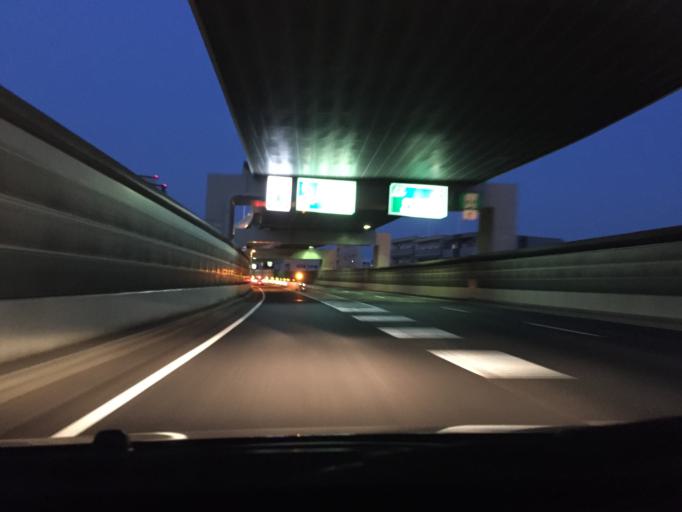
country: JP
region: Kanagawa
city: Yokohama
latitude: 35.4328
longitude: 139.6202
